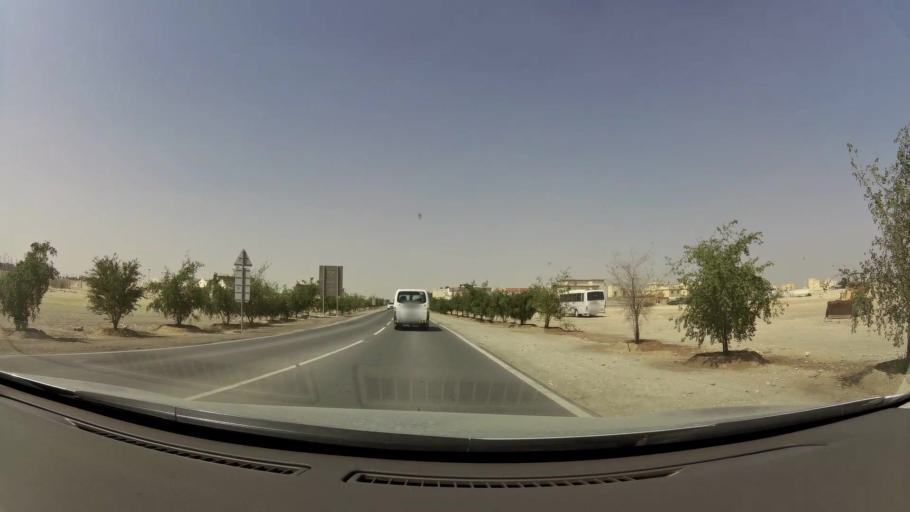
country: QA
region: Baladiyat Umm Salal
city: Umm Salal Muhammad
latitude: 25.3717
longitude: 51.4217
